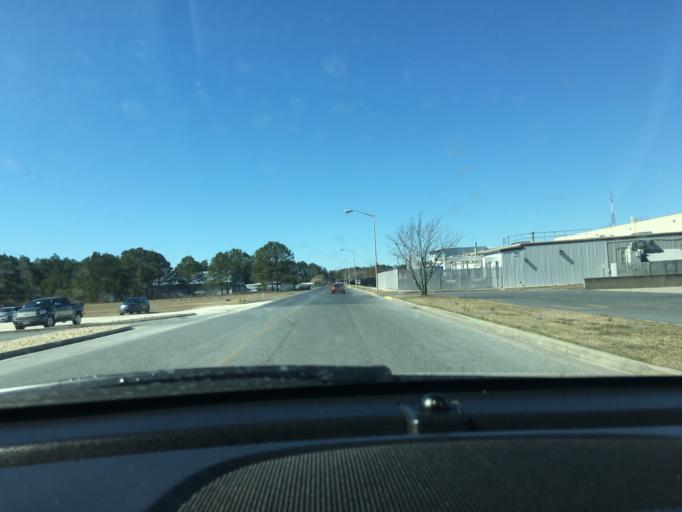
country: US
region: Maryland
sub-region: Wicomico County
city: Salisbury
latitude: 38.4026
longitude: -75.5734
